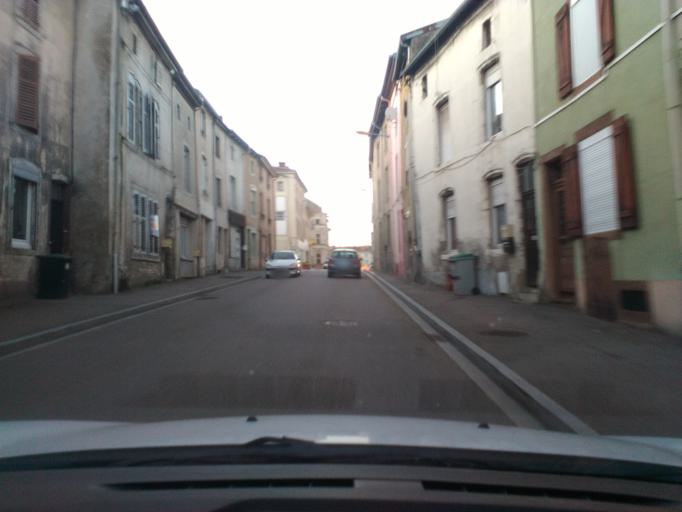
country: FR
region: Lorraine
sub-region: Departement des Vosges
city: Charmes
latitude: 48.3700
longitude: 6.2947
